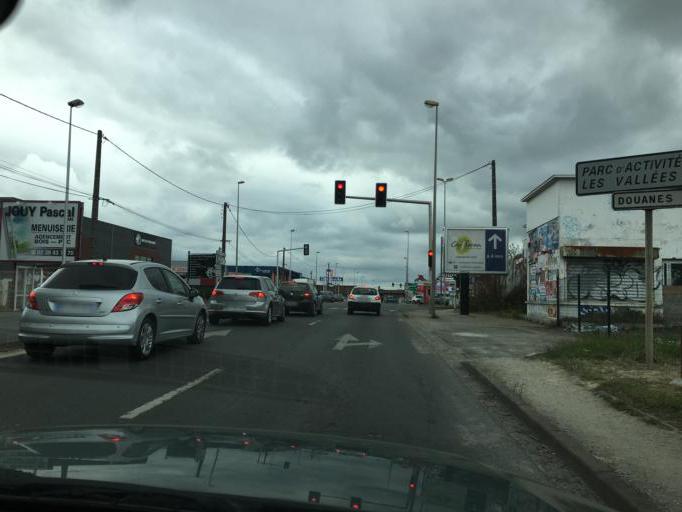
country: FR
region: Centre
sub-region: Departement du Loiret
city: Saran
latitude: 47.9428
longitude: 1.8929
